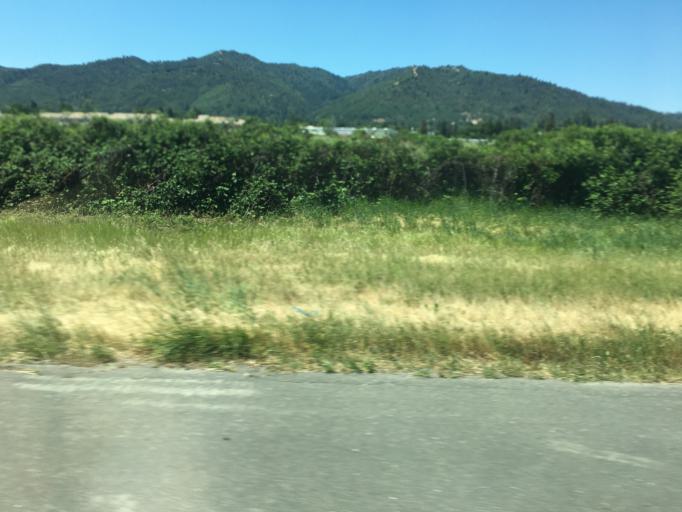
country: US
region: California
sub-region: Mendocino County
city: Ukiah
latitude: 39.1625
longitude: -123.1997
